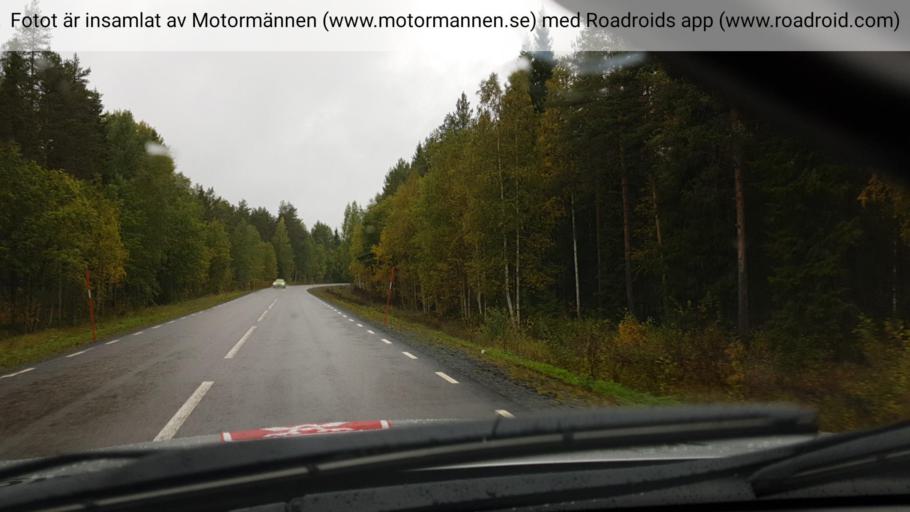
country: SE
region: Norrbotten
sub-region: Lulea Kommun
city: Sodra Sunderbyn
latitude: 65.8201
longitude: 21.9038
